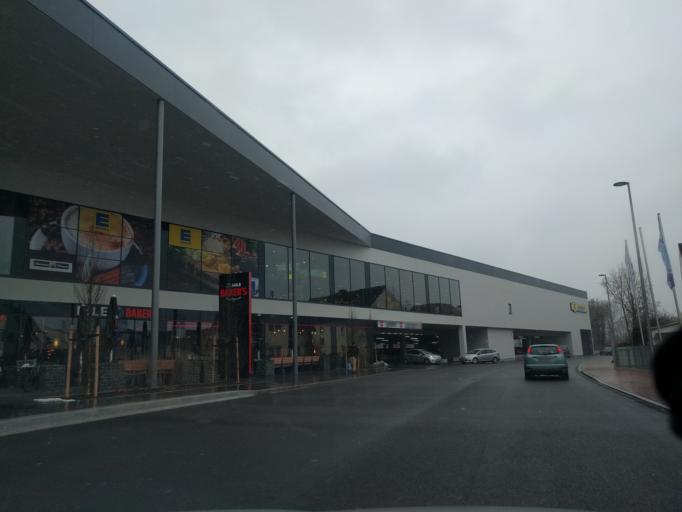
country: DE
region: Bavaria
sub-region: Swabia
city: Donauwoerth
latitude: 48.7163
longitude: 10.7687
